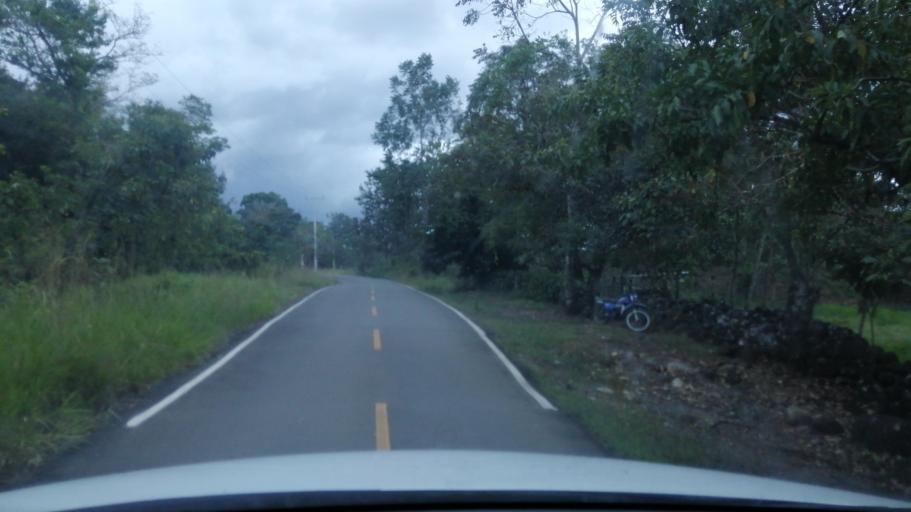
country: PA
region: Chiriqui
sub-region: Distrito Dolega
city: Pueblo Nuevo
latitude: 8.5951
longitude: -82.4131
